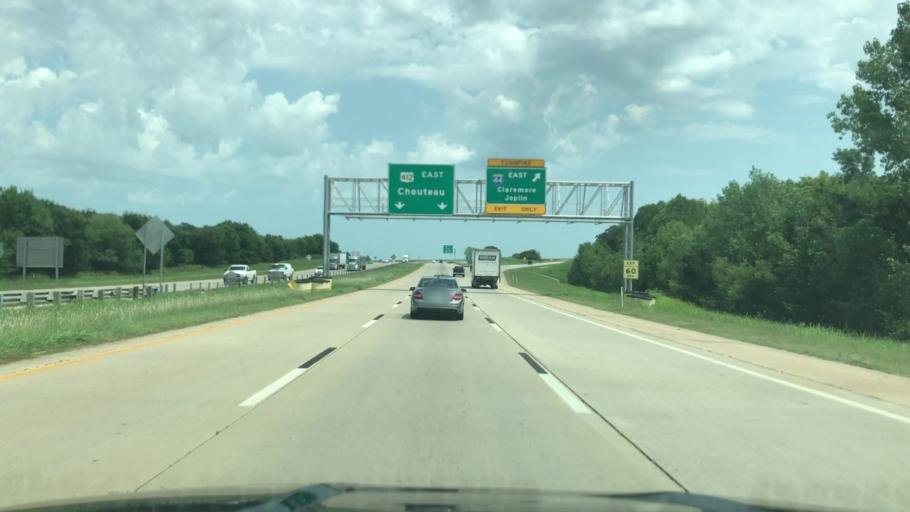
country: US
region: Oklahoma
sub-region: Rogers County
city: Catoosa
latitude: 36.1629
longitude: -95.7439
